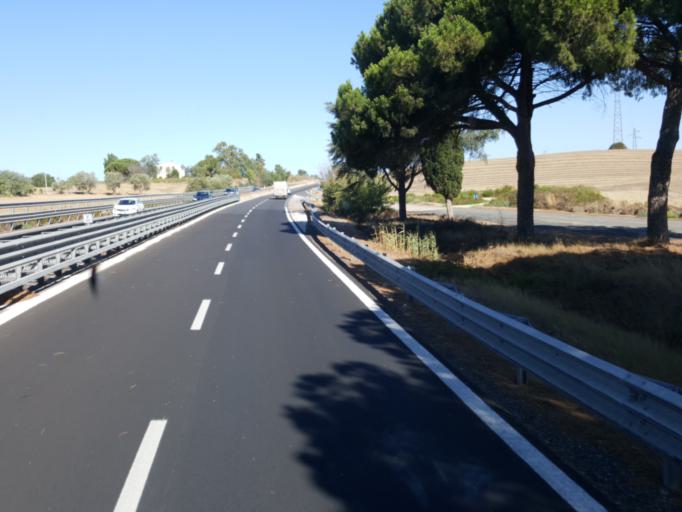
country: IT
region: Latium
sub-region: Provincia di Viterbo
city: Montalto di Castro
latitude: 42.3578
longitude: 11.5883
